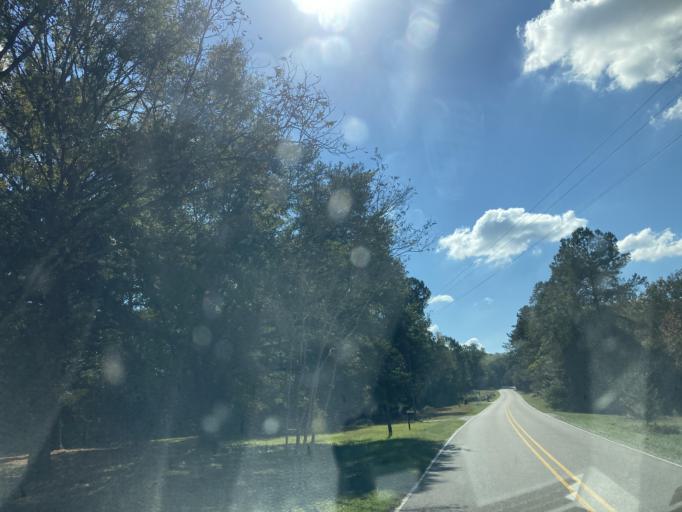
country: US
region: Mississippi
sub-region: Lamar County
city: Sumrall
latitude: 31.3503
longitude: -89.5544
